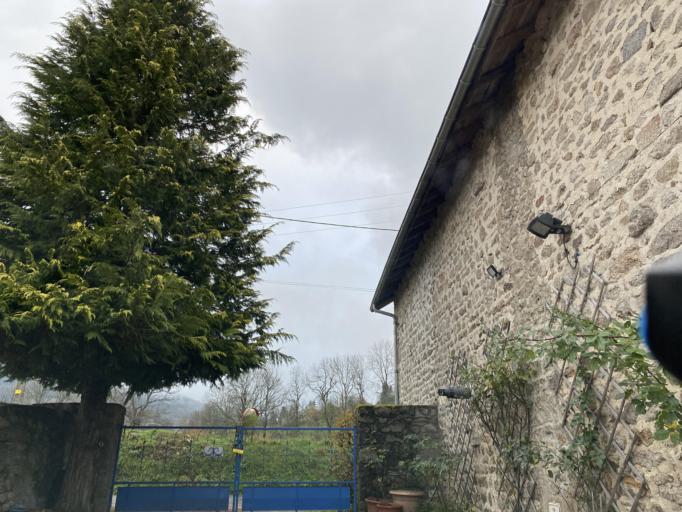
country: FR
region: Auvergne
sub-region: Departement du Puy-de-Dome
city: Celles-sur-Durolle
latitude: 45.7686
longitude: 3.6625
